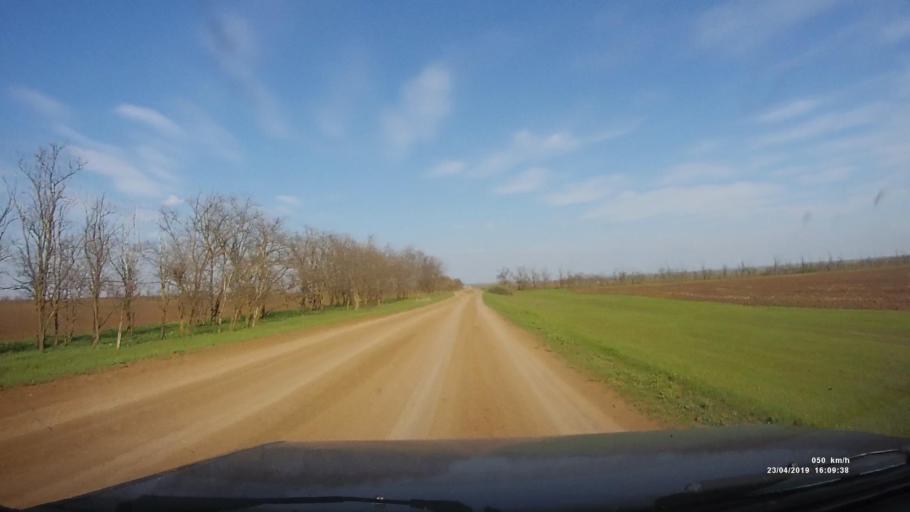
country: RU
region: Rostov
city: Remontnoye
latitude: 46.4816
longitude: 43.1131
